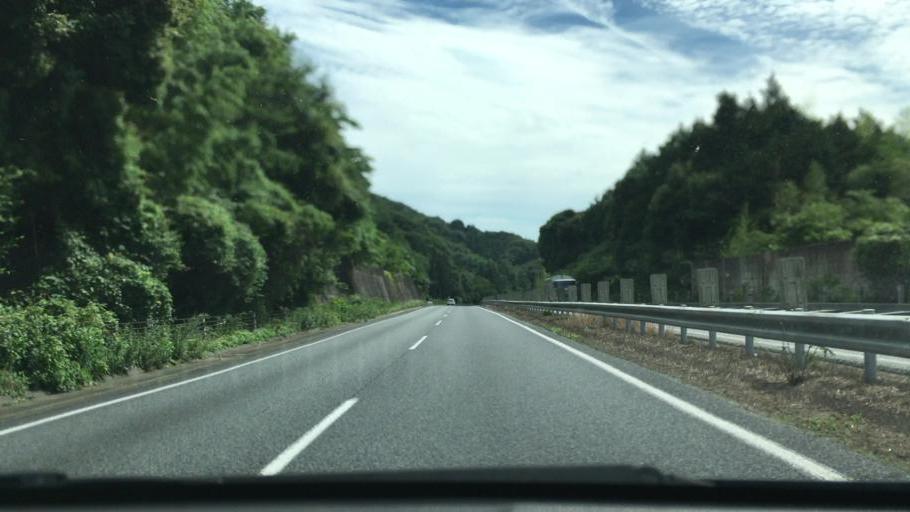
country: JP
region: Yamaguchi
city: Ogori-shimogo
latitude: 34.1272
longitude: 131.4212
